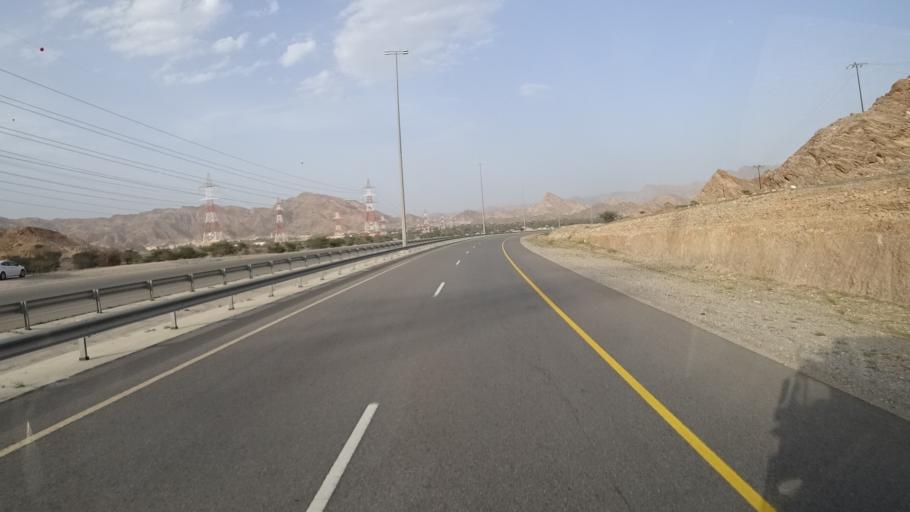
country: OM
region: Muhafazat Masqat
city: Muscat
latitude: 23.3665
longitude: 58.6365
